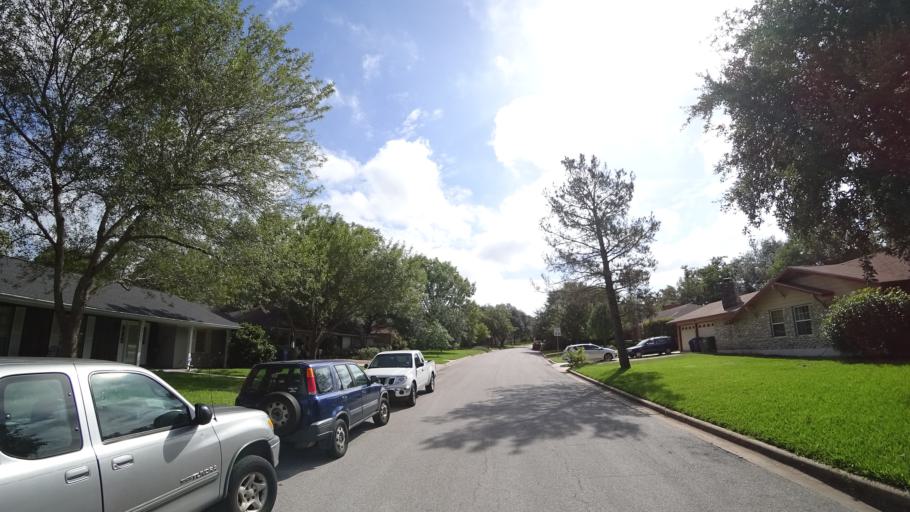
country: US
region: Texas
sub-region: Travis County
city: West Lake Hills
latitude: 30.3515
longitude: -97.7403
